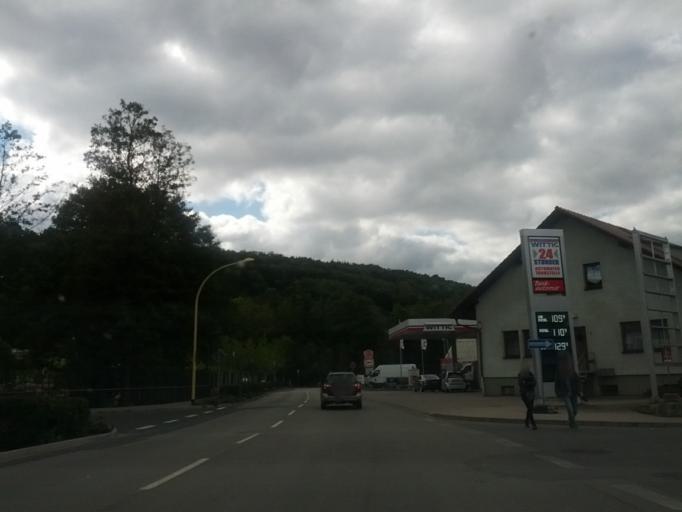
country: DE
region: Thuringia
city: Schmalkalden
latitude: 50.7198
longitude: 10.4419
